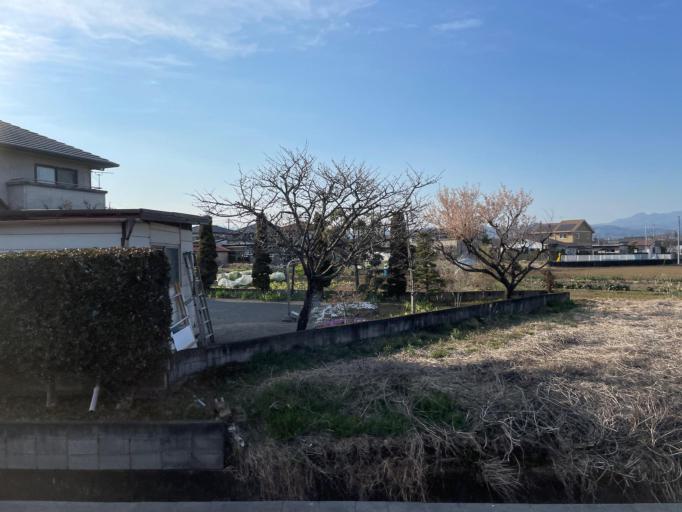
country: JP
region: Gunma
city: Annaka
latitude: 36.3056
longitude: 138.8728
